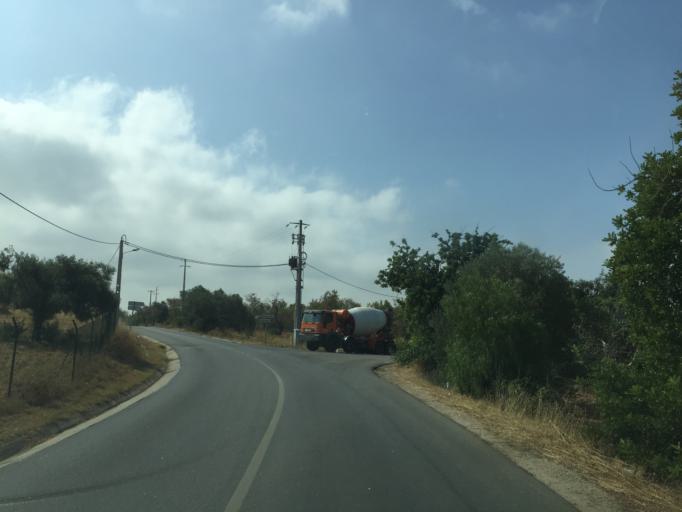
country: PT
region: Faro
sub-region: Olhao
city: Olhao
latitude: 37.0792
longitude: -7.8910
